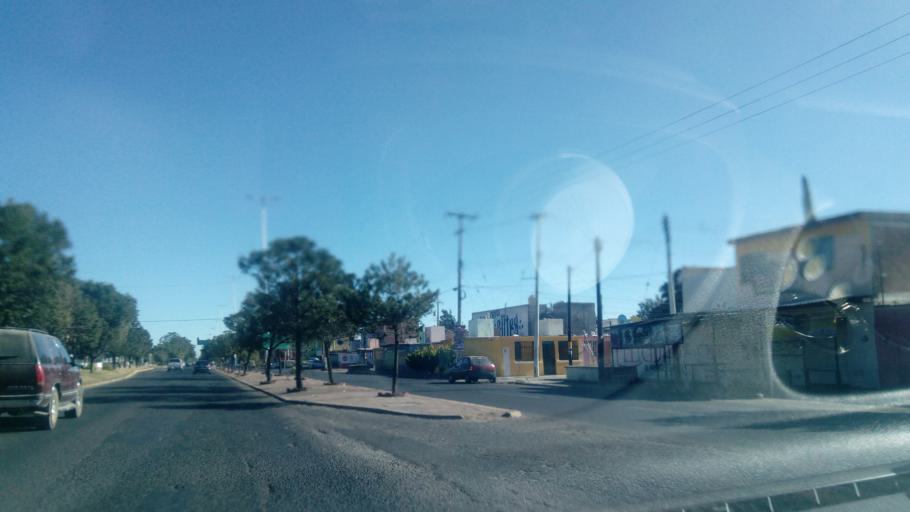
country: MX
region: Durango
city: Victoria de Durango
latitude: 24.0489
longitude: -104.6214
